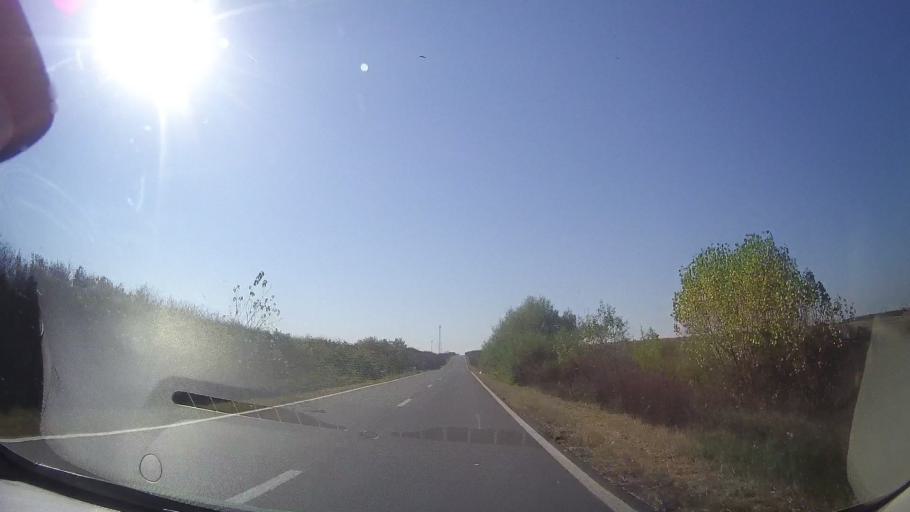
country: RO
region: Timis
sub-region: Comuna Belint
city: Belint
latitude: 45.7705
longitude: 21.7296
